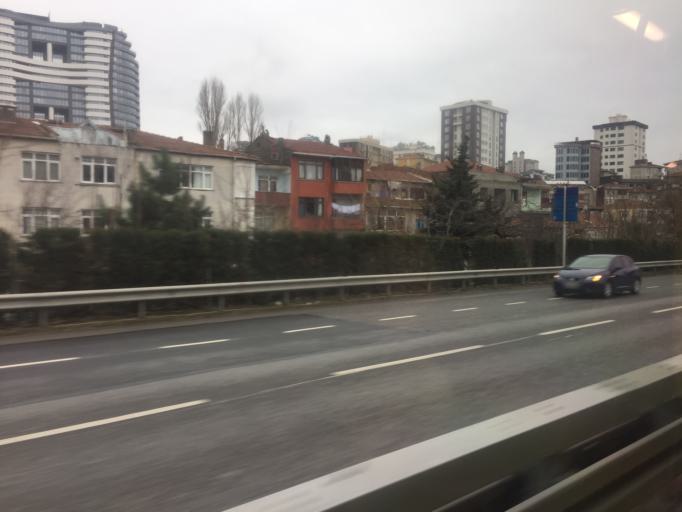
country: TR
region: Istanbul
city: UEskuedar
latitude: 40.9925
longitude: 29.0438
